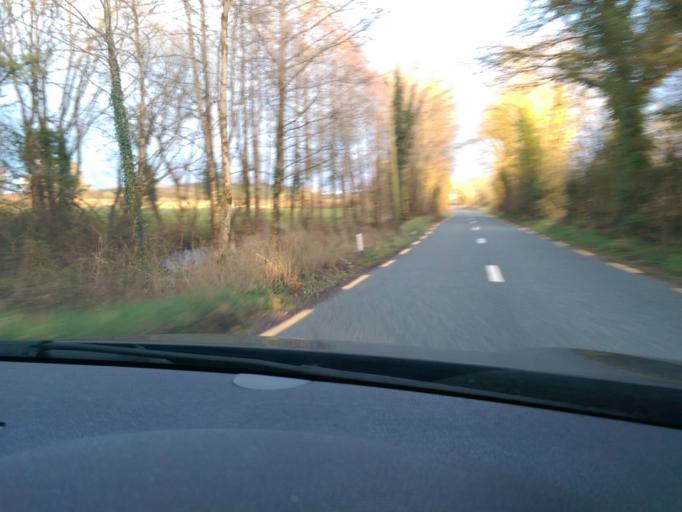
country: IE
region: Connaught
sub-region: Sligo
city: Ballymote
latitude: 54.0302
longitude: -8.5864
